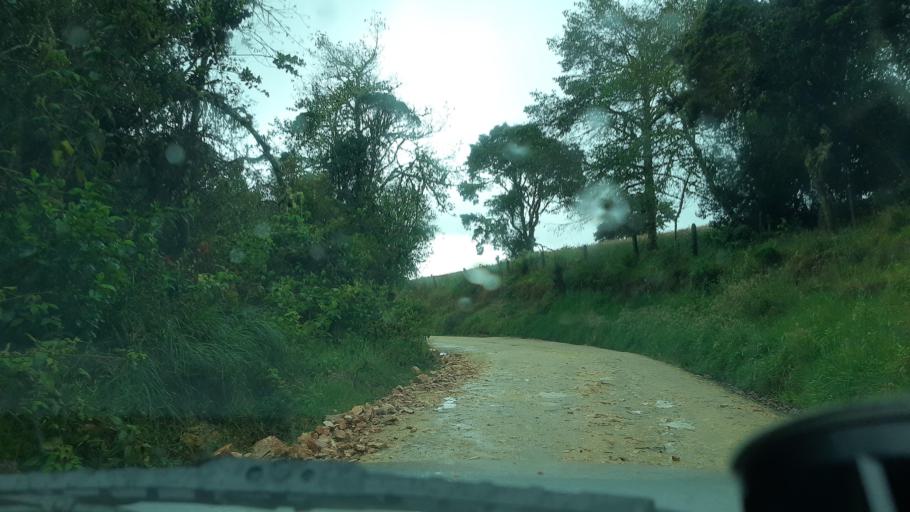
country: CO
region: Cundinamarca
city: Villapinzon
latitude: 5.2073
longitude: -73.5602
